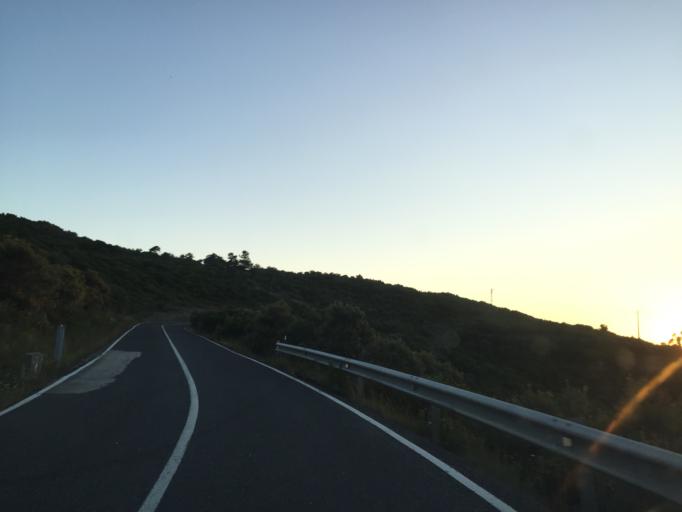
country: PT
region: Santarem
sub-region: Ourem
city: Fatima
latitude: 39.6319
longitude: -8.6357
